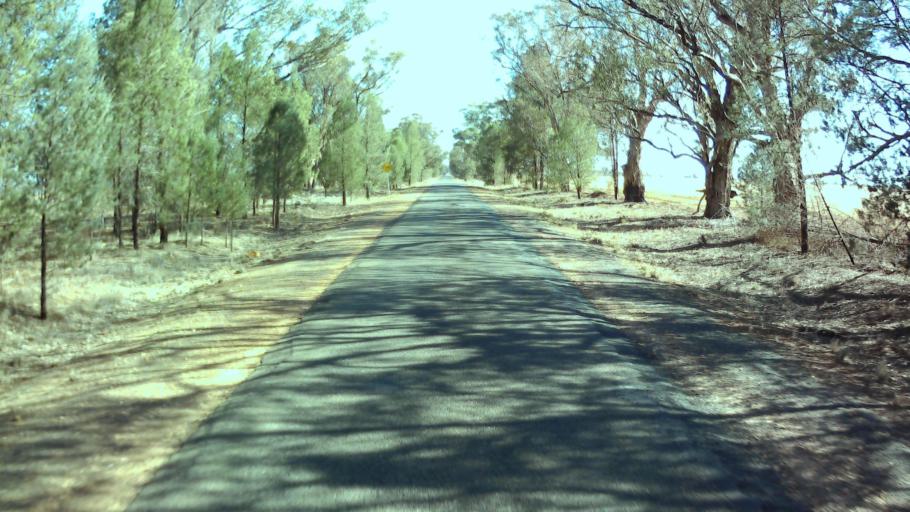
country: AU
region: New South Wales
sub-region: Weddin
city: Grenfell
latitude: -33.8085
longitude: 147.9544
